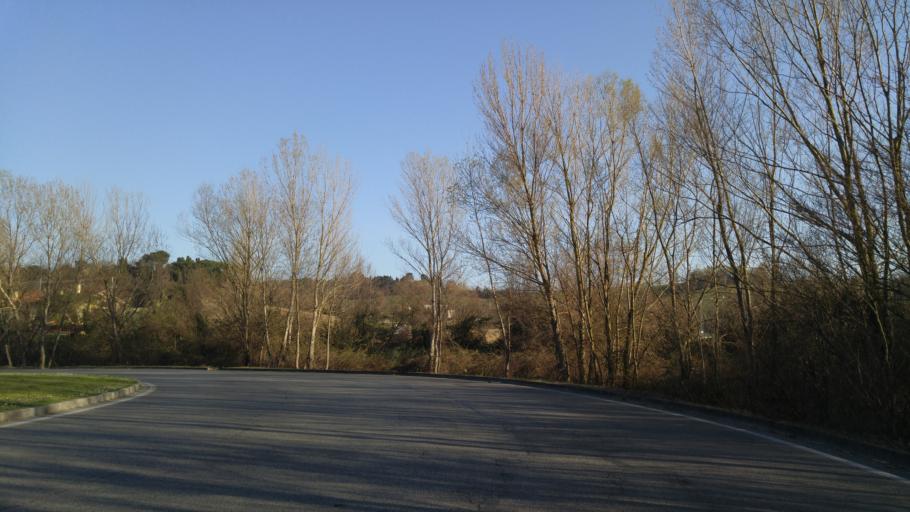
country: IT
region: The Marches
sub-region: Provincia di Pesaro e Urbino
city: Pesaro
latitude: 43.8875
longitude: 12.9069
